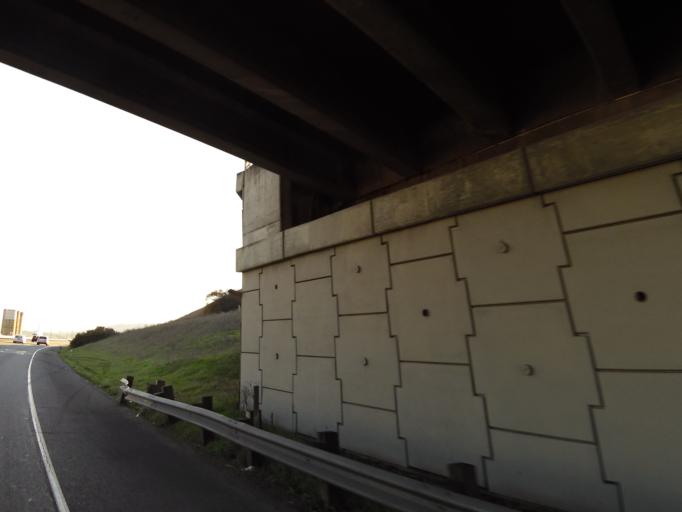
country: US
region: California
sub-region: Santa Clara County
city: Gilroy
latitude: 36.9613
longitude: -121.5512
